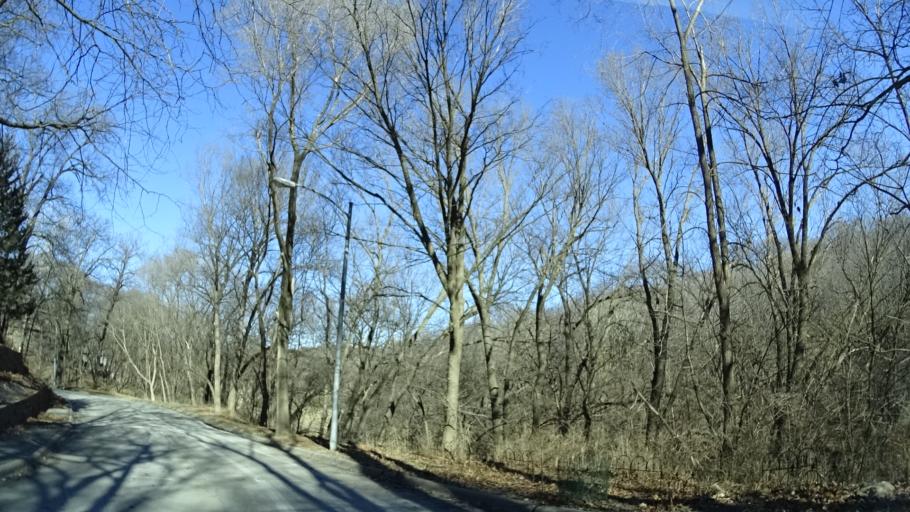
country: US
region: Nebraska
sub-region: Sarpy County
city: Bellevue
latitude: 41.1519
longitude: -95.8971
